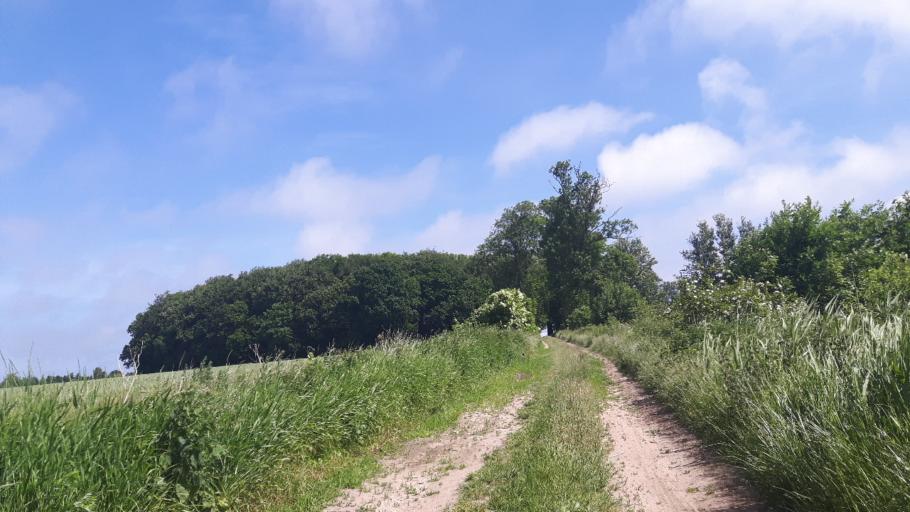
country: PL
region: West Pomeranian Voivodeship
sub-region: Powiat slawienski
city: Darlowo
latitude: 54.4685
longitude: 16.4663
